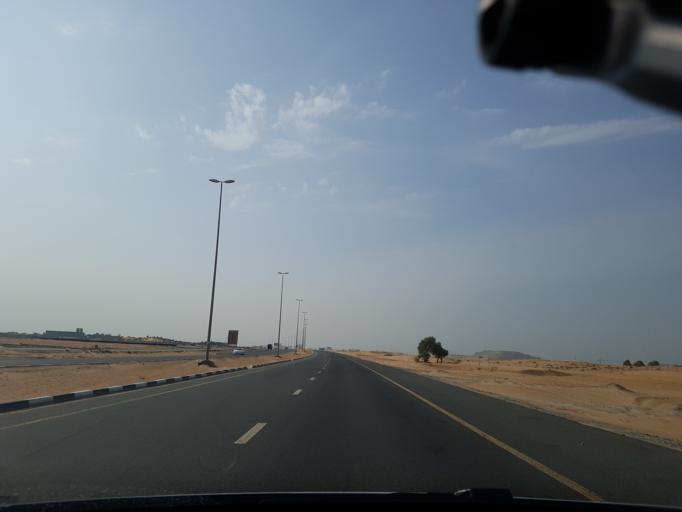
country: AE
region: Ajman
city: Ajman
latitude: 25.4083
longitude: 55.5730
